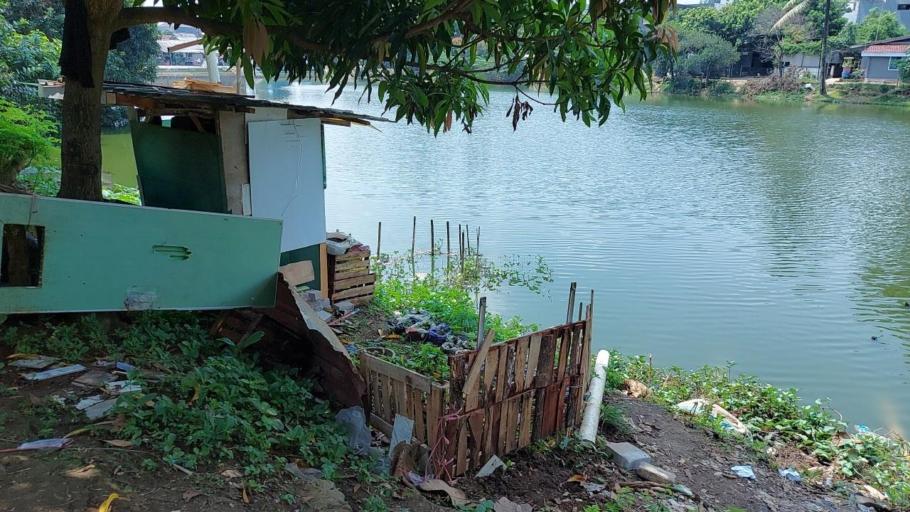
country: ID
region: West Java
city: Cibinong
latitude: -6.4709
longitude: 106.8472
